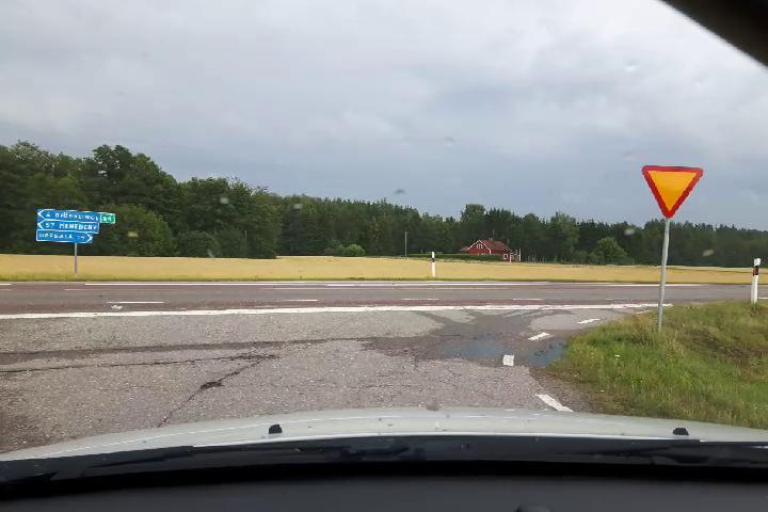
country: SE
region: Uppsala
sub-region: Osthammars Kommun
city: Bjorklinge
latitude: 59.9686
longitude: 17.5797
